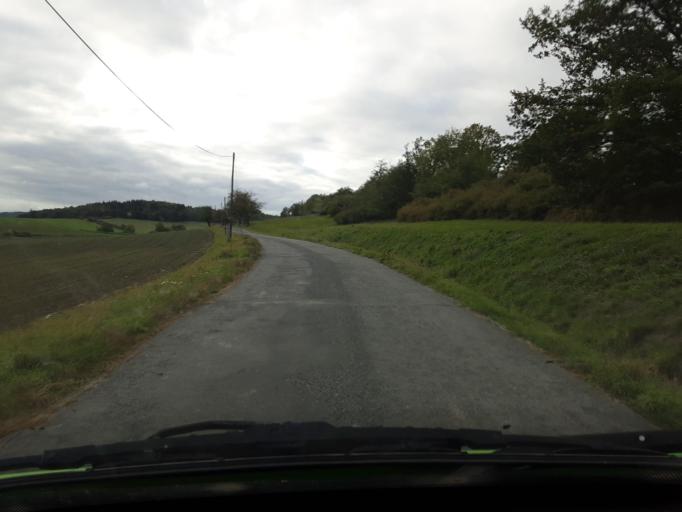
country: CZ
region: Plzensky
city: Janovice nad Uhlavou
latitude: 49.4275
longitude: 13.1728
